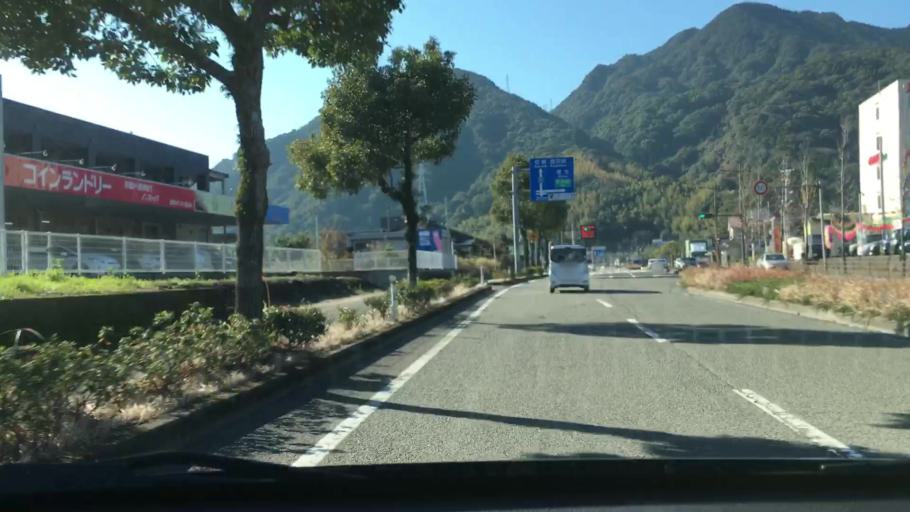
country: JP
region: Kagoshima
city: Kajiki
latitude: 31.7072
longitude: 130.6143
